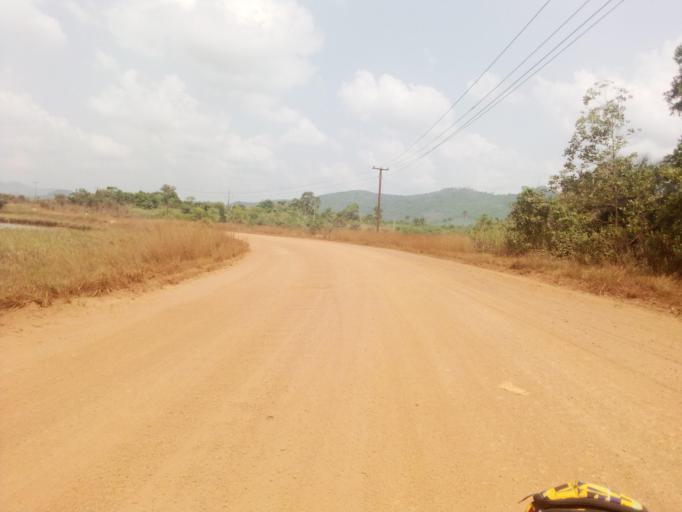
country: SL
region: Southern Province
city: Mogbwemo
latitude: 7.6684
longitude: -12.2780
